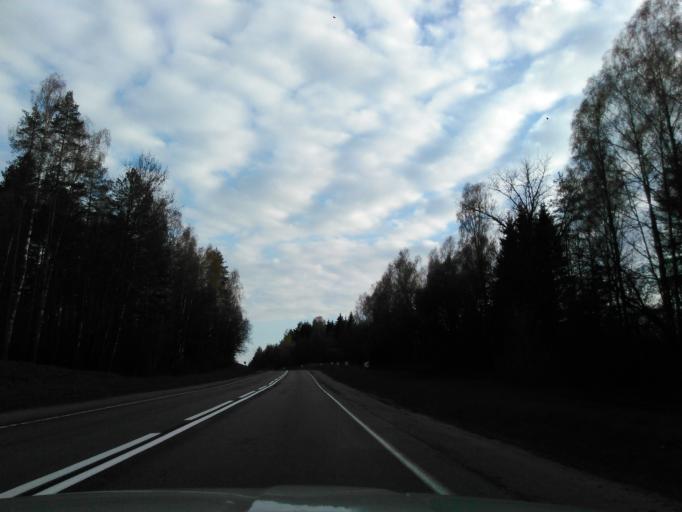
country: BY
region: Minsk
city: Plyeshchanitsy
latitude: 54.3343
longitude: 27.8760
